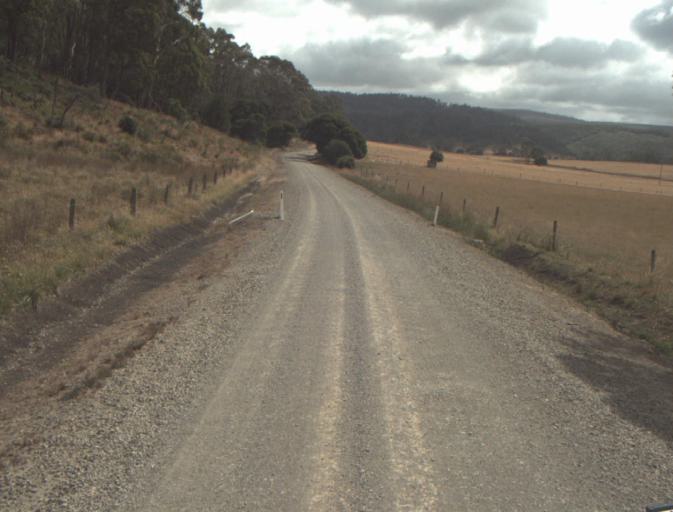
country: AU
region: Tasmania
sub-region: Northern Midlands
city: Evandale
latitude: -41.4784
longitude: 147.4445
